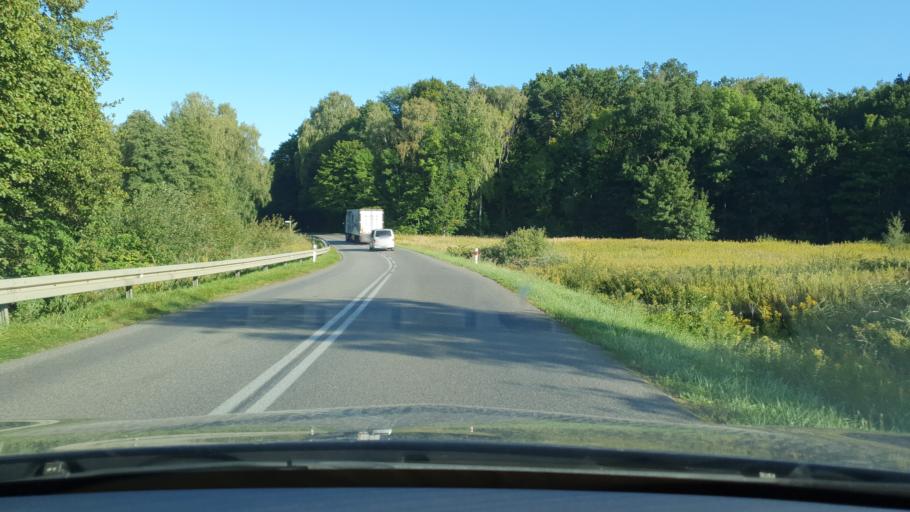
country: PL
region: West Pomeranian Voivodeship
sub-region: Powiat kamienski
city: Golczewo
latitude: 53.8213
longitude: 14.9606
